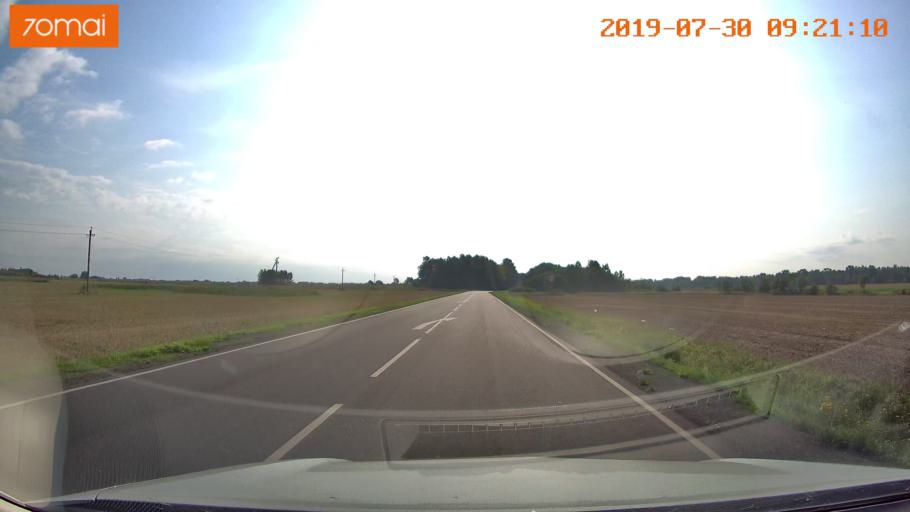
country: RU
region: Kaliningrad
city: Nesterov
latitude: 54.6360
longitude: 22.6252
